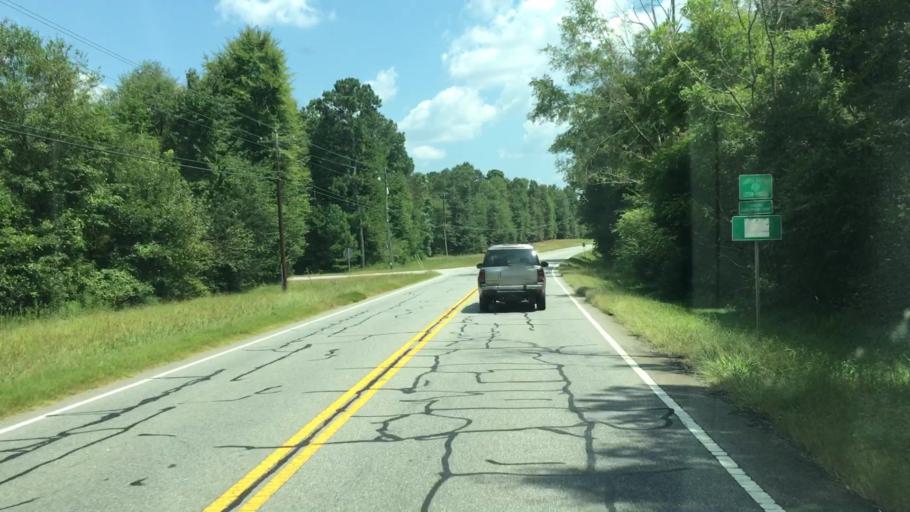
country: US
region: Georgia
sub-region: Barrow County
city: Statham
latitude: 33.9085
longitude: -83.5866
